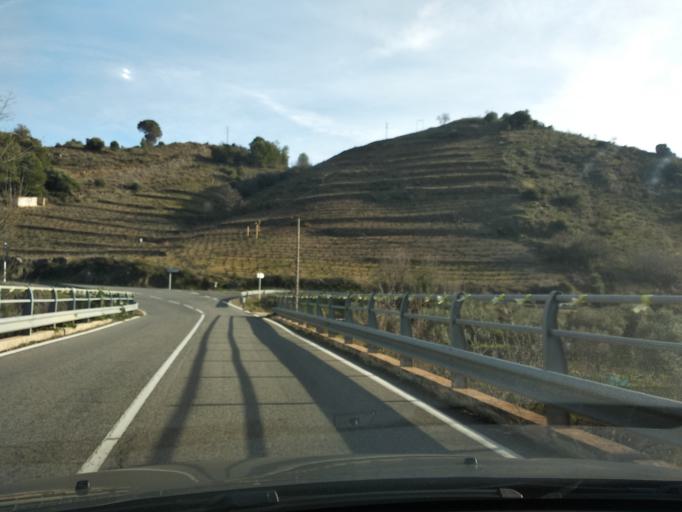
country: ES
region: Catalonia
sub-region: Provincia de Tarragona
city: Margalef
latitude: 41.2228
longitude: 0.7655
